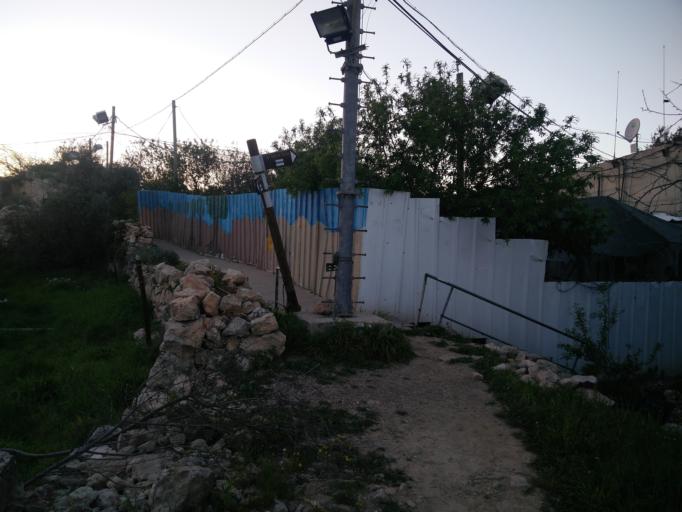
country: PS
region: West Bank
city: Hebron
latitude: 31.5245
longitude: 35.1024
